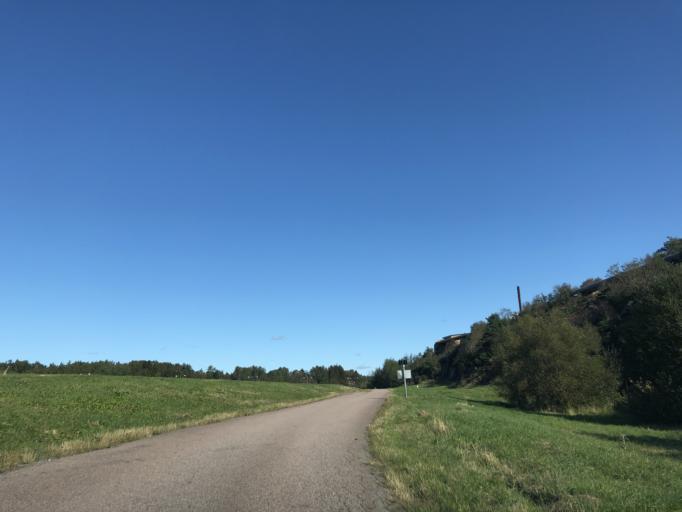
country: SE
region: Vaestra Goetaland
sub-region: Goteborg
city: Torslanda
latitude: 57.7148
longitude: 11.8067
